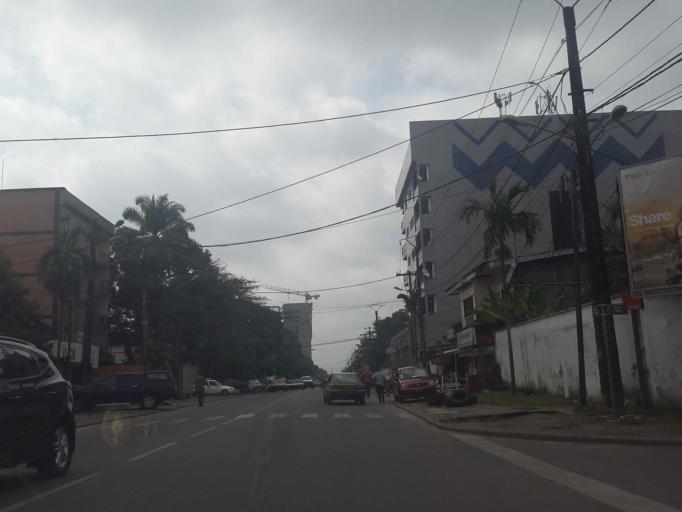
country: CM
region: Littoral
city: Douala
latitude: 4.0290
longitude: 9.6968
